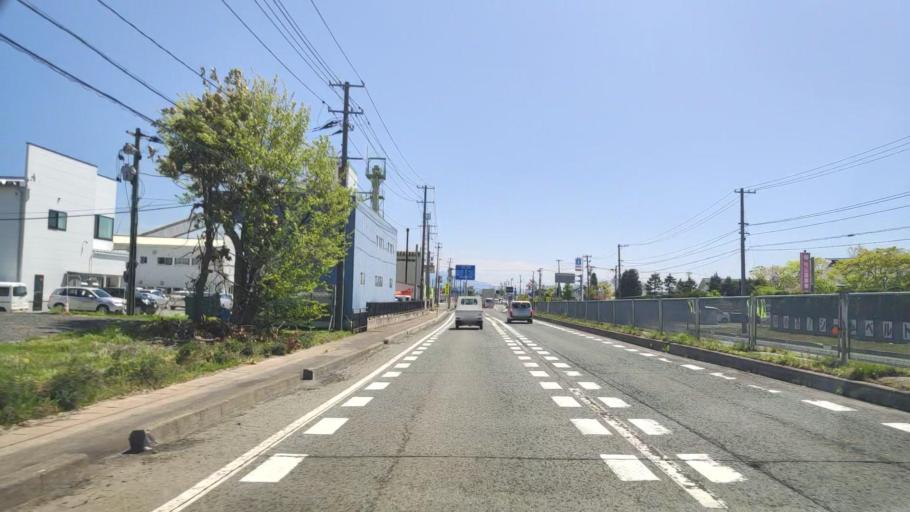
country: JP
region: Yamagata
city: Higashine
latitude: 38.4842
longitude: 140.3831
